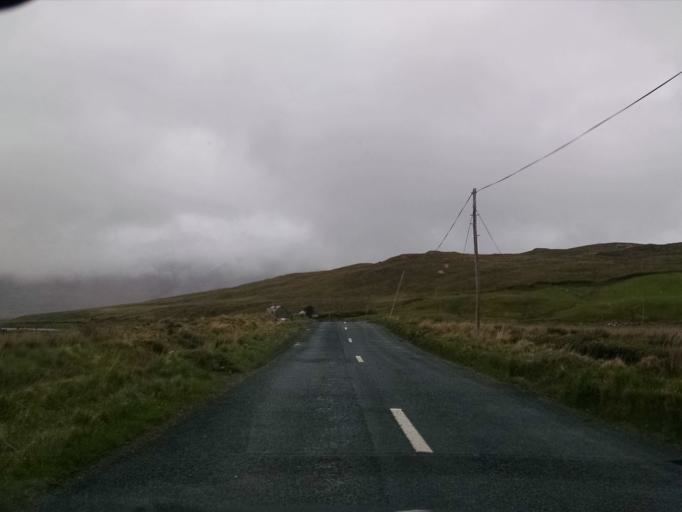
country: IE
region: Connaught
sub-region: County Galway
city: Clifden
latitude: 53.4939
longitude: -9.7373
